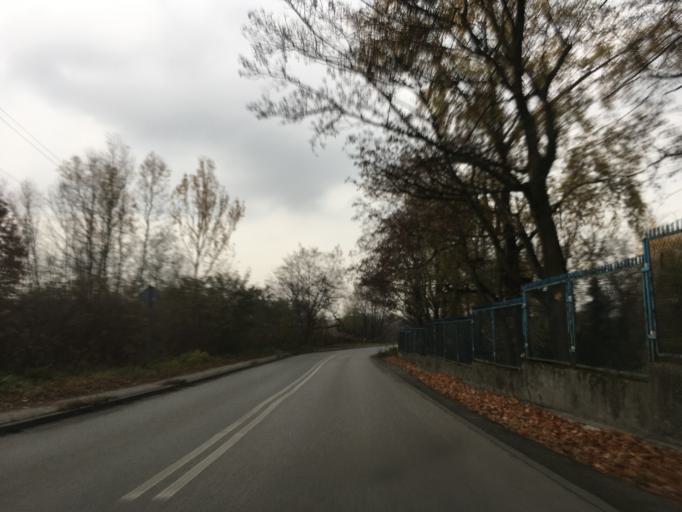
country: PL
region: Masovian Voivodeship
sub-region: Powiat piaseczynski
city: Zalesie Gorne
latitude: 52.0482
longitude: 21.0062
